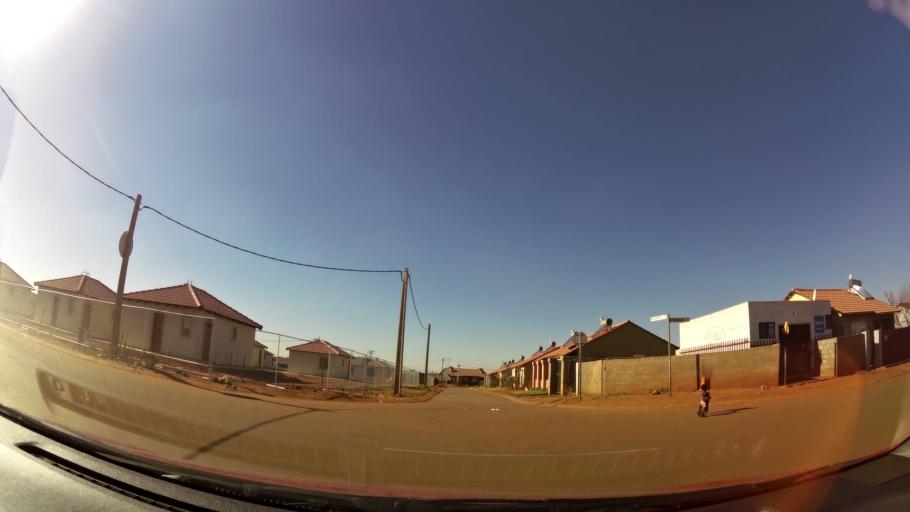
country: ZA
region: Gauteng
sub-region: City of Johannesburg Metropolitan Municipality
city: Soweto
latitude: -26.2331
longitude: 27.8020
